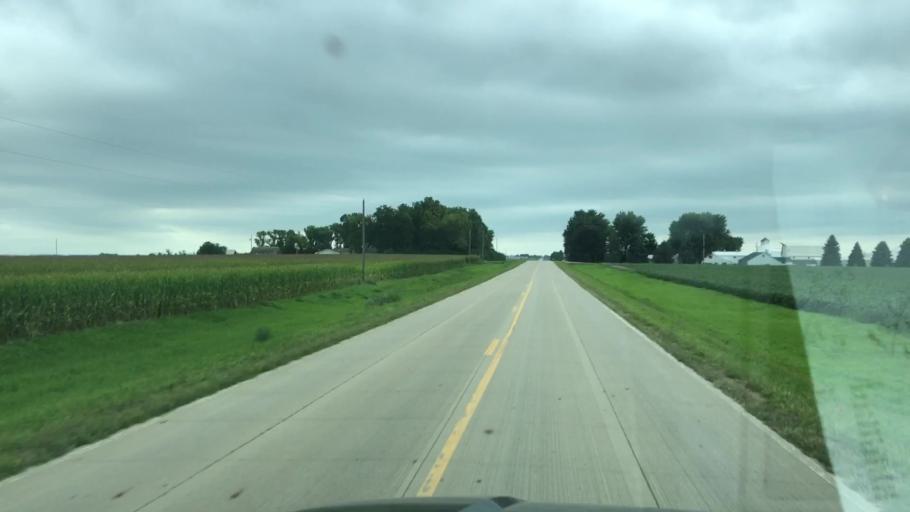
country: US
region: Iowa
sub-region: O'Brien County
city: Sheldon
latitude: 43.1445
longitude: -95.9795
